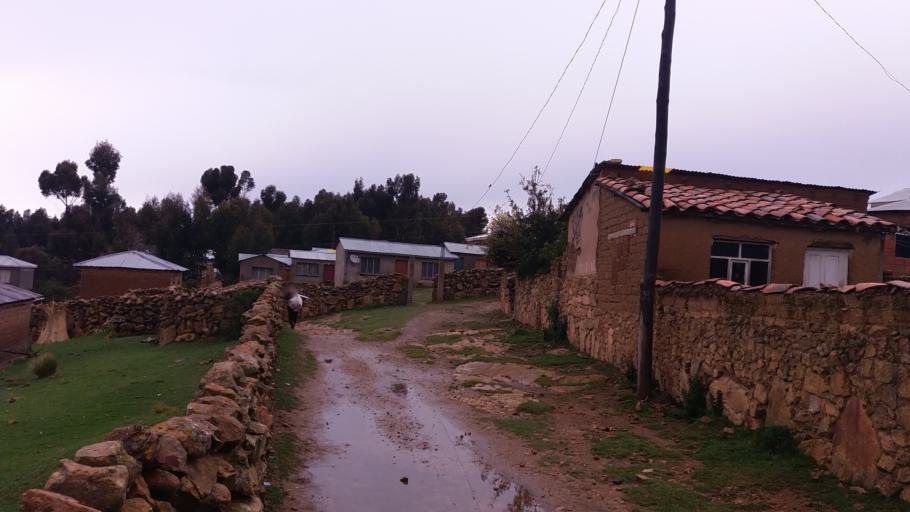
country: BO
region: La Paz
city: Yumani
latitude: -16.0358
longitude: -69.1499
